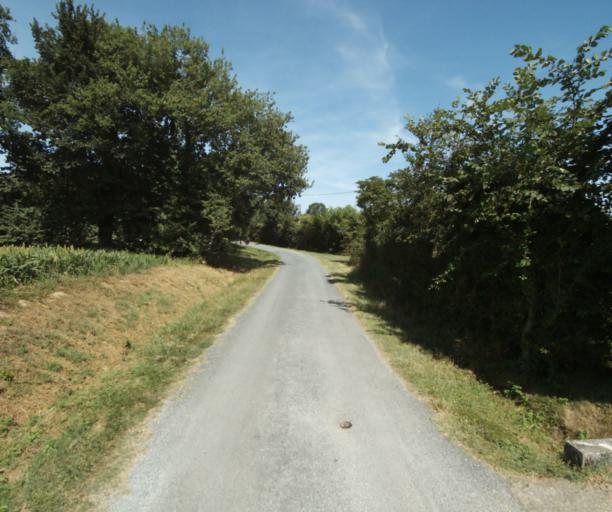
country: FR
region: Midi-Pyrenees
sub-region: Departement du Tarn
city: Puylaurens
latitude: 43.5401
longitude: 2.0123
